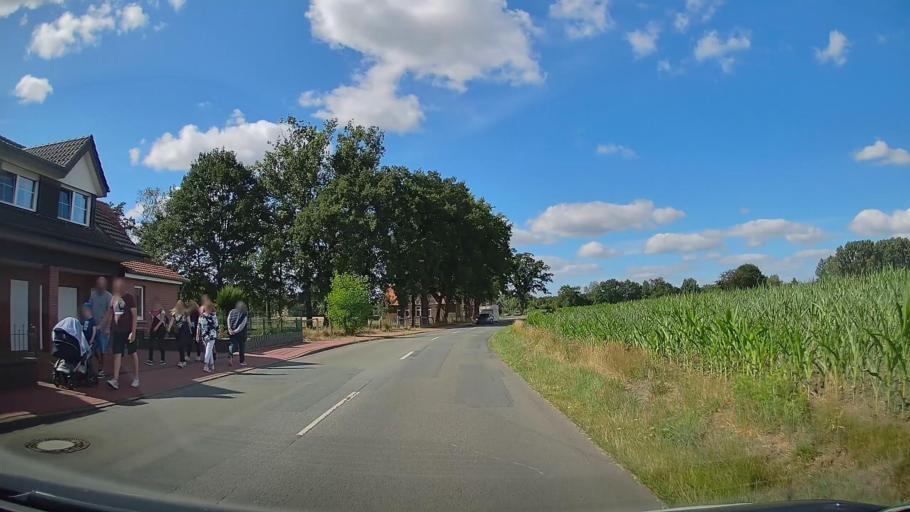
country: DE
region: Lower Saxony
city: Rieste
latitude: 52.4863
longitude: 7.9932
